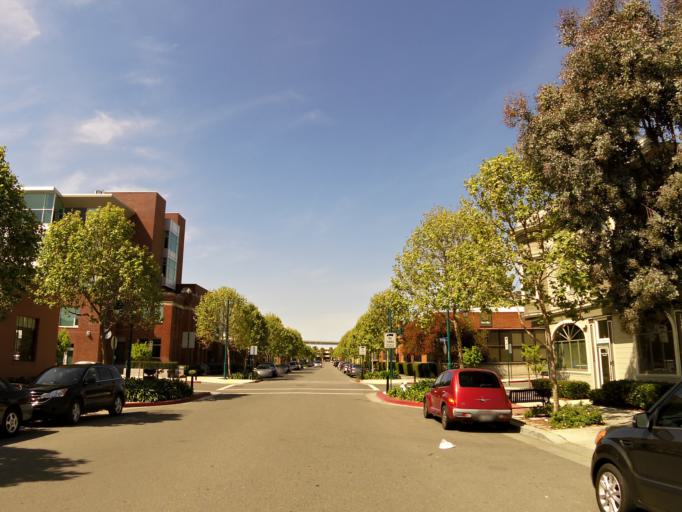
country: US
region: California
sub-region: Alameda County
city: Emeryville
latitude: 37.8311
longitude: -122.2865
